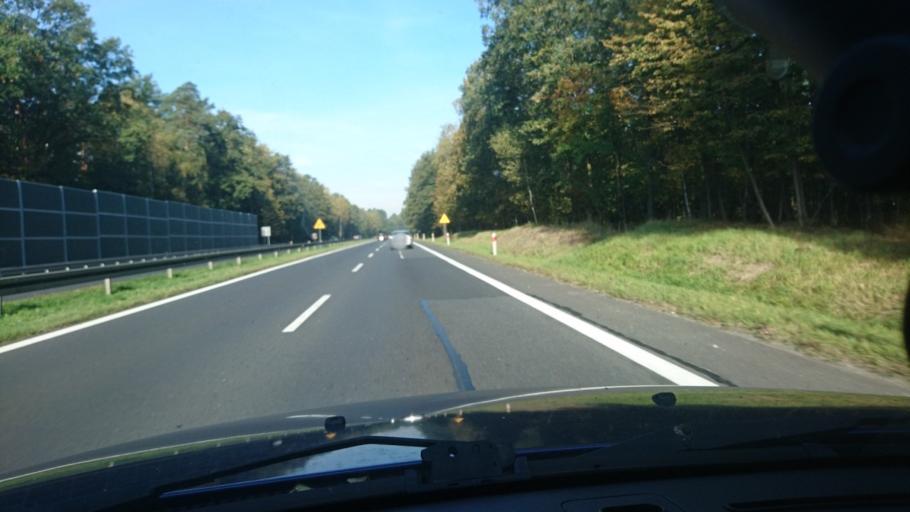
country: PL
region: Silesian Voivodeship
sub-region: Powiat pszczynski
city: Piasek
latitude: 50.0197
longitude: 18.9467
